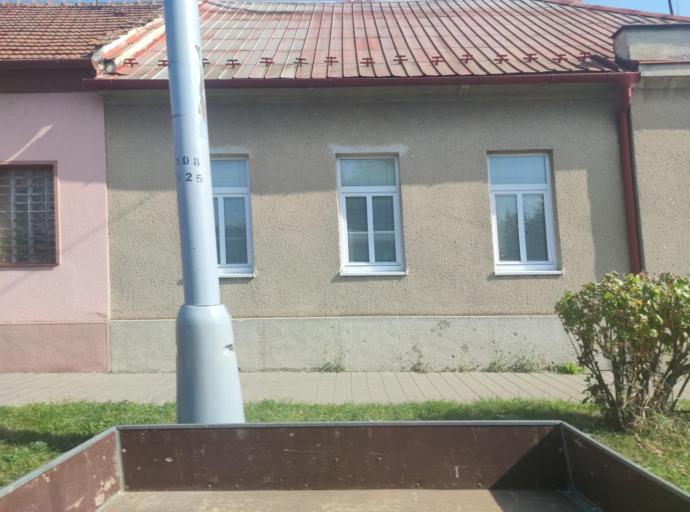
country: CZ
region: South Moravian
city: Podoli
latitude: 49.1751
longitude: 16.6859
